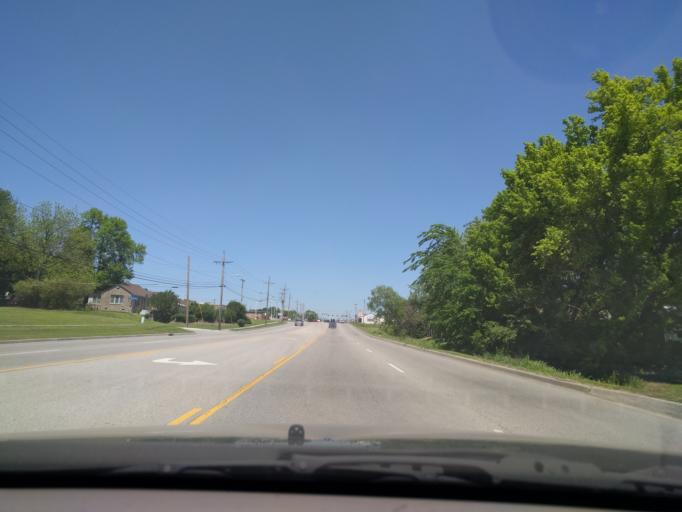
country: US
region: Oklahoma
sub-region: Tulsa County
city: Broken Arrow
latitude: 36.0574
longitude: -95.7974
